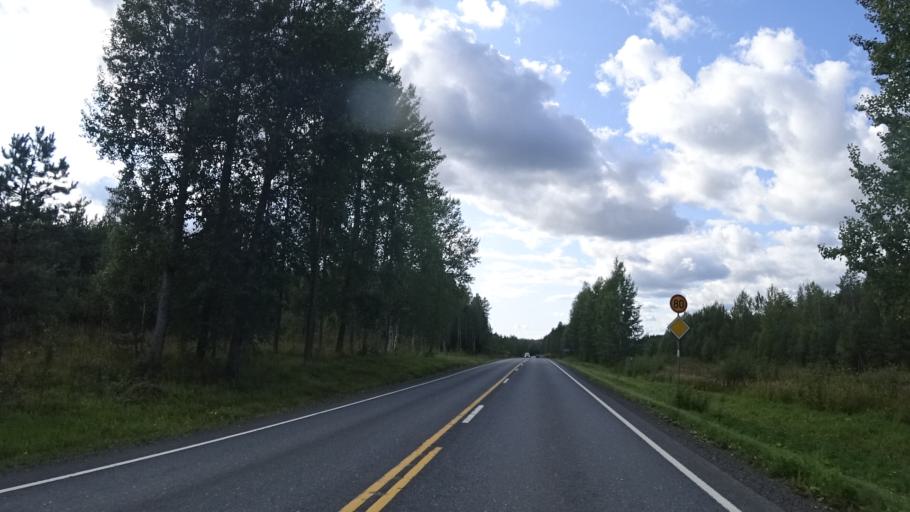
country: RU
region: Republic of Karelia
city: Vyartsilya
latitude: 62.1755
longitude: 30.5483
